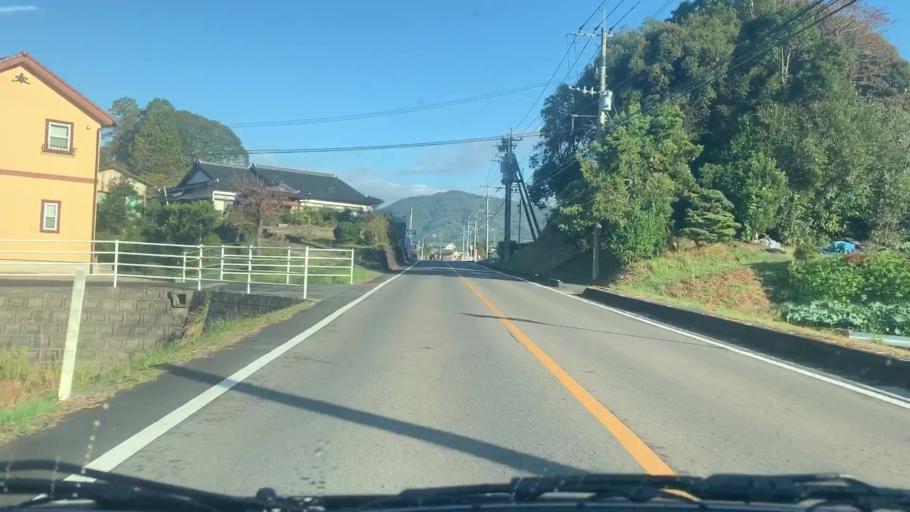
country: JP
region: Saga Prefecture
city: Takeocho-takeo
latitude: 33.2127
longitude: 130.0288
